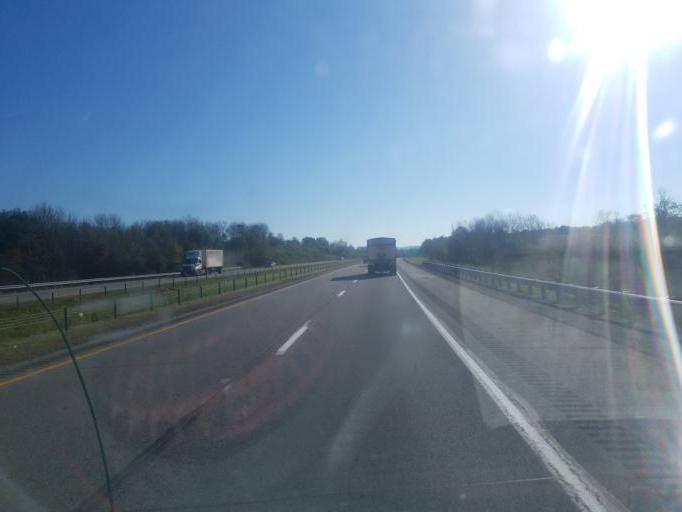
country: US
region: Pennsylvania
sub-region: Cambria County
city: Loretto
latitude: 40.4640
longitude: -78.6423
